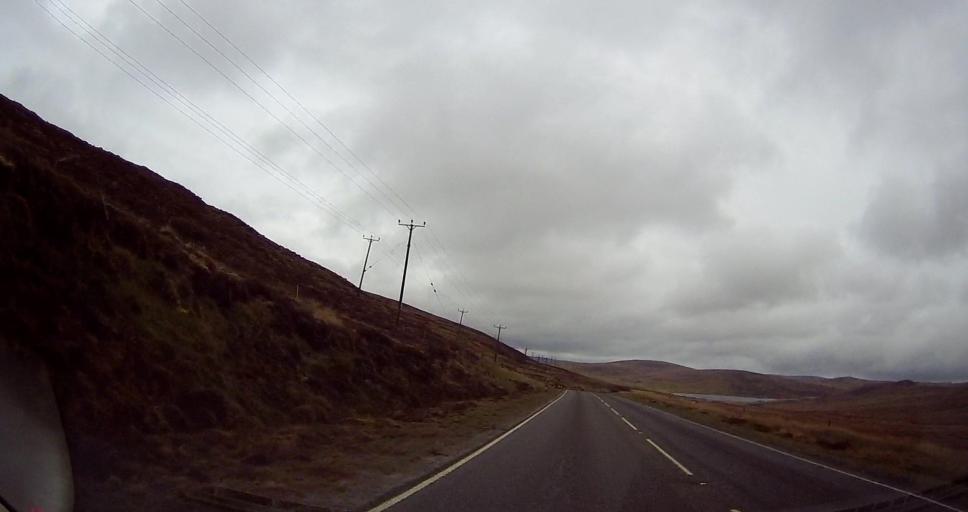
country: GB
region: Scotland
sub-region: Shetland Islands
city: Lerwick
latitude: 60.3321
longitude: -1.2542
